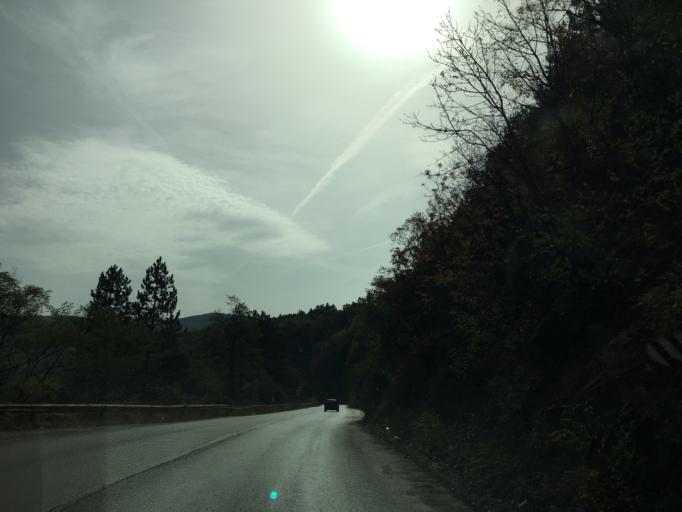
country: BG
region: Sofia-Capital
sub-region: Stolichna Obshtina
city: Sofia
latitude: 42.5771
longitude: 23.4277
